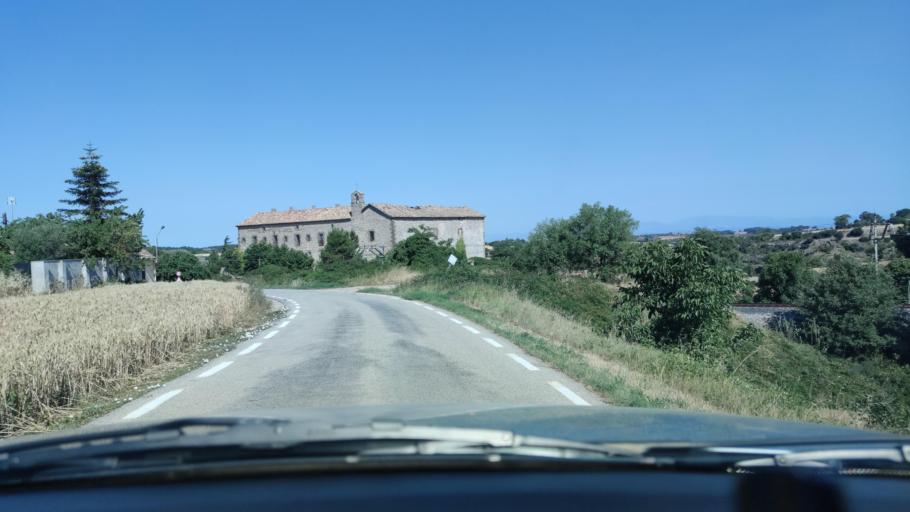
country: ES
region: Catalonia
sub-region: Provincia de Lleida
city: Sant Guim de Freixenet
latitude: 41.6484
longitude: 1.4079
